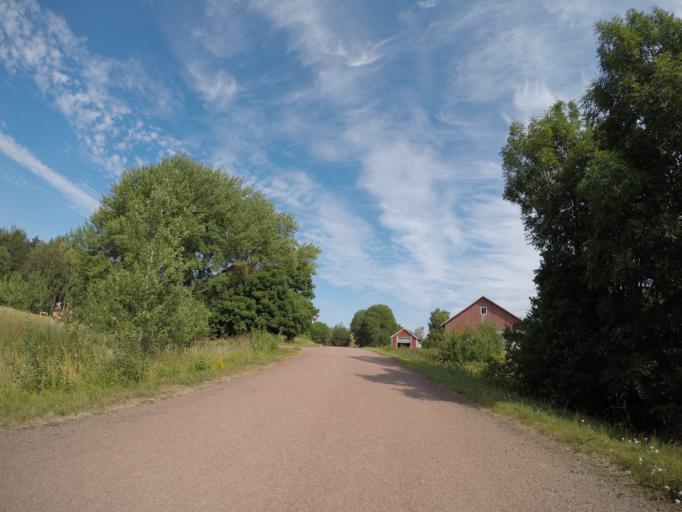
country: AX
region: Alands landsbygd
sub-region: Finstroem
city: Finstroem
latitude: 60.2051
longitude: 19.8746
